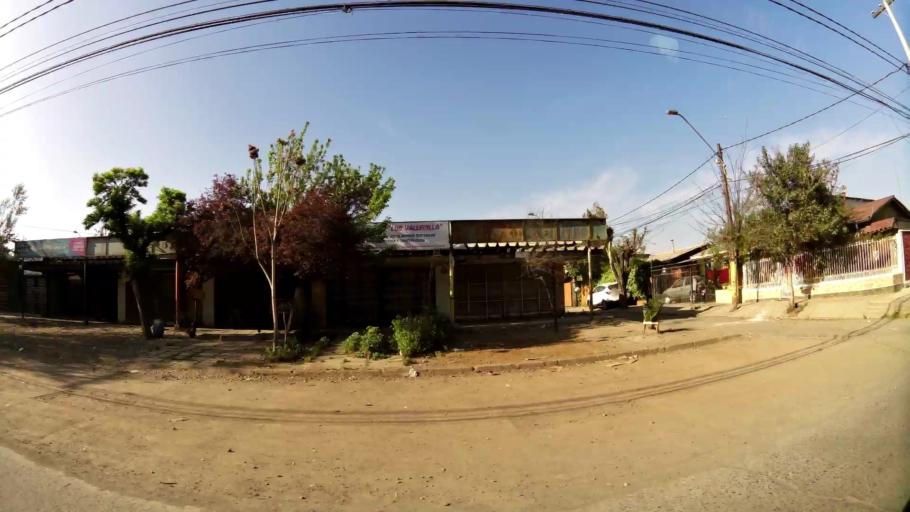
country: CL
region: Santiago Metropolitan
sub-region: Provincia de Santiago
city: Santiago
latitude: -33.3898
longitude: -70.6668
